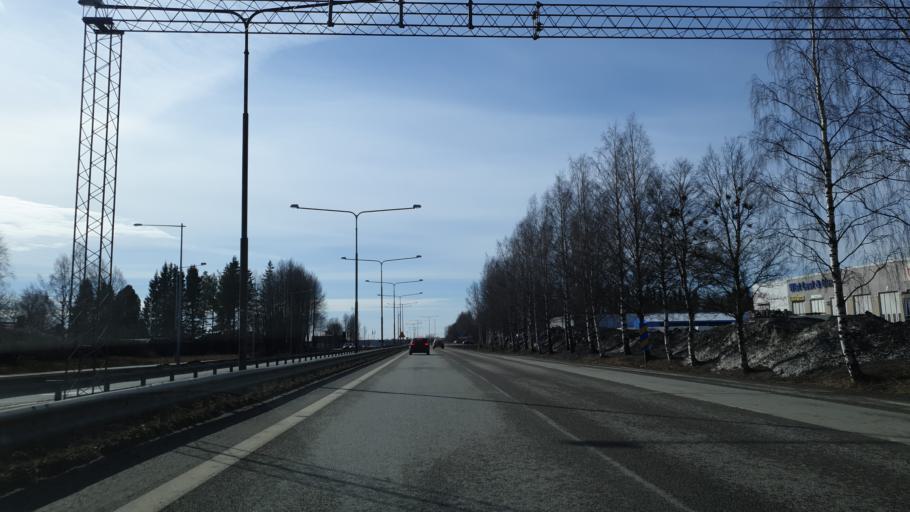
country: SE
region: Vaesterbotten
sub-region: Umea Kommun
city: Umea
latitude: 63.8142
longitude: 20.2494
